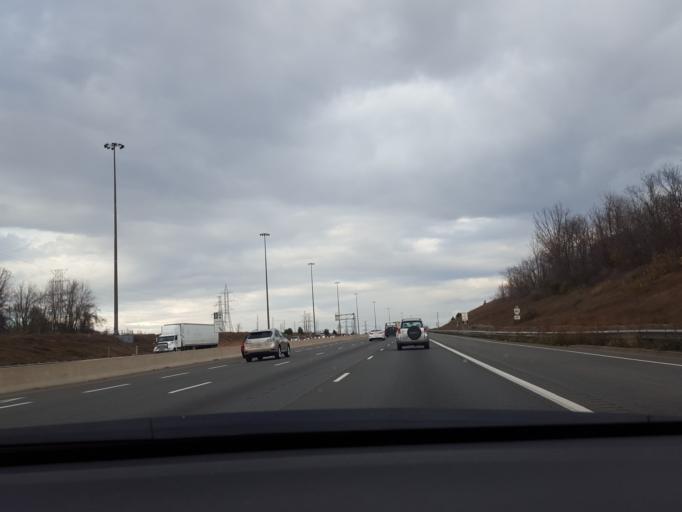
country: CA
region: Ontario
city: Mississauga
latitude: 43.5717
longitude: -79.6740
